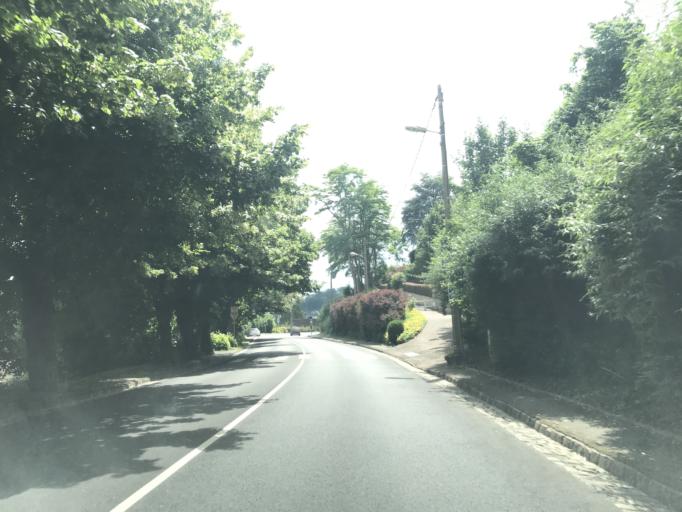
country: FR
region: Haute-Normandie
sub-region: Departement de la Seine-Maritime
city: Mont-Saint-Aignan
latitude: 49.4623
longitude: 1.0869
